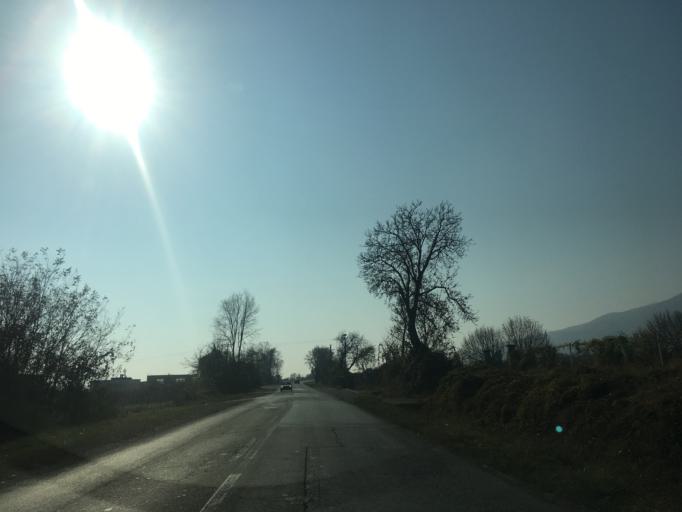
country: XK
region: Gjakova
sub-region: Komuna e Decanit
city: Strellc i Eperm
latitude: 42.6080
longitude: 20.3018
